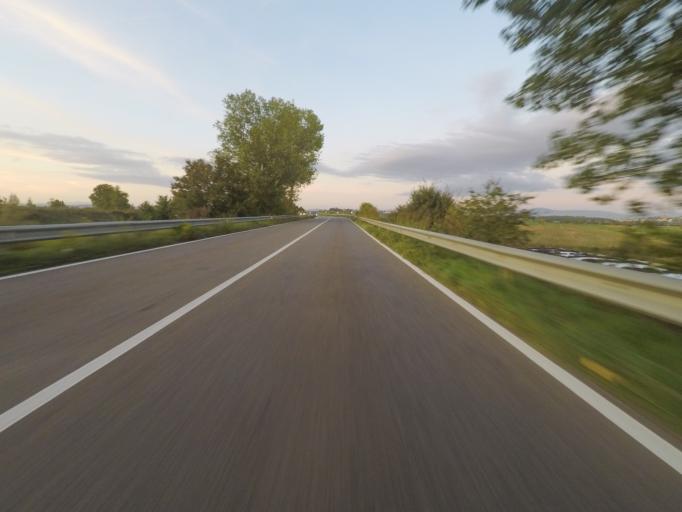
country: IT
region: Tuscany
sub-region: Provincia di Siena
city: Sinalunga
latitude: 43.1950
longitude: 11.7609
